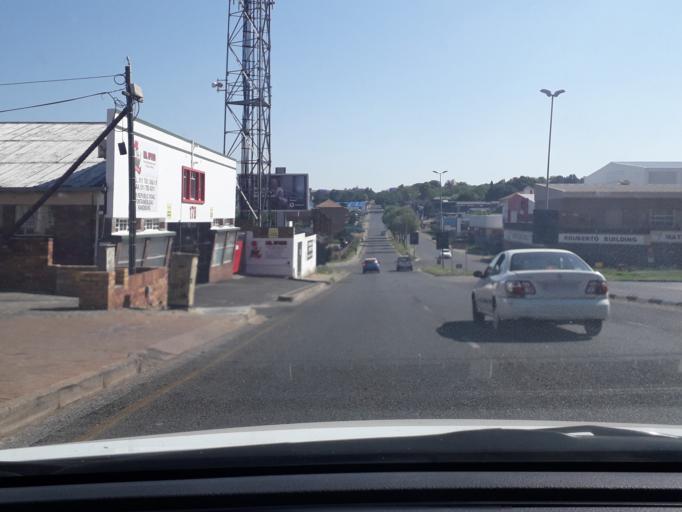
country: ZA
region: Gauteng
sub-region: City of Johannesburg Metropolitan Municipality
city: Roodepoort
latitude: -26.1074
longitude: 27.9748
